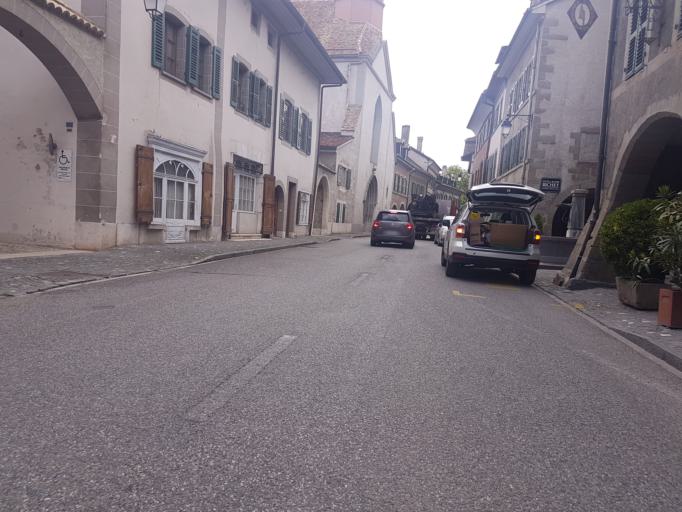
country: CH
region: Vaud
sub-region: Nyon District
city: Coppet
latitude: 46.3164
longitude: 6.1933
